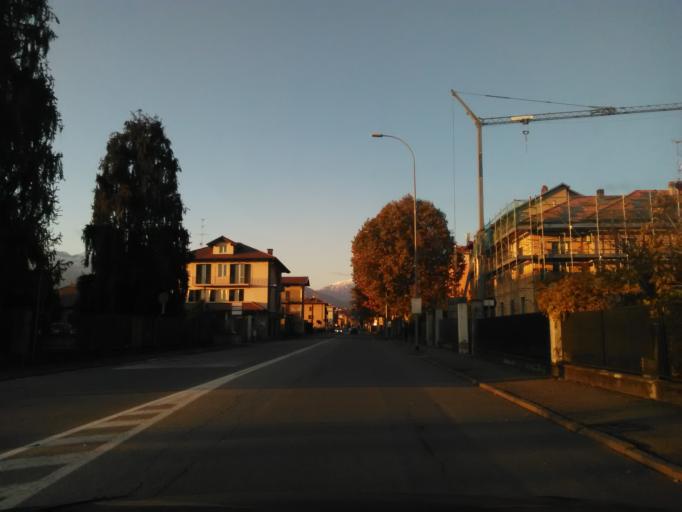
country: IT
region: Piedmont
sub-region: Provincia di Biella
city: Ponderano
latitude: 45.5454
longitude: 8.0523
